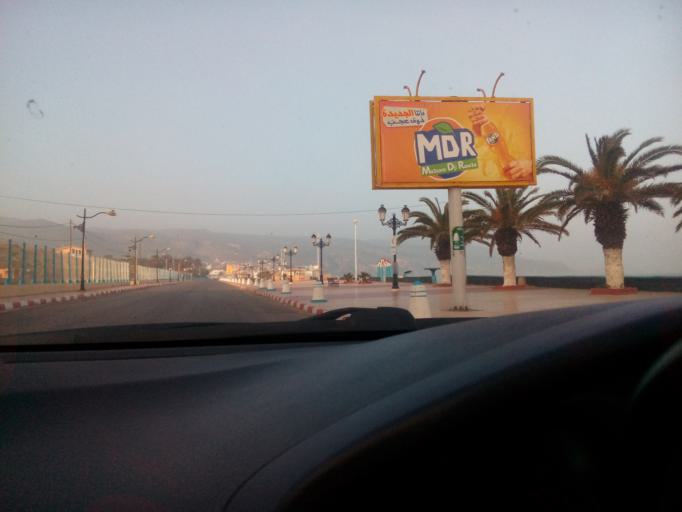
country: DZ
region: Oran
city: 'Ain el Turk
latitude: 35.7060
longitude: -0.8863
